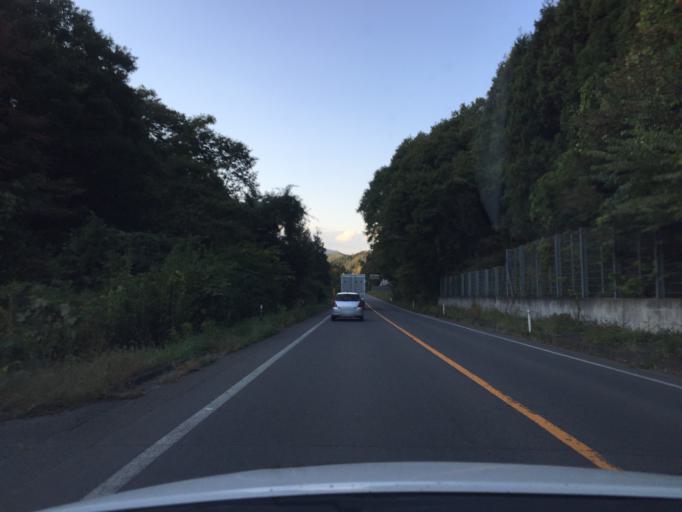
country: JP
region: Fukushima
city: Sukagawa
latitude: 37.2827
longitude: 140.5444
